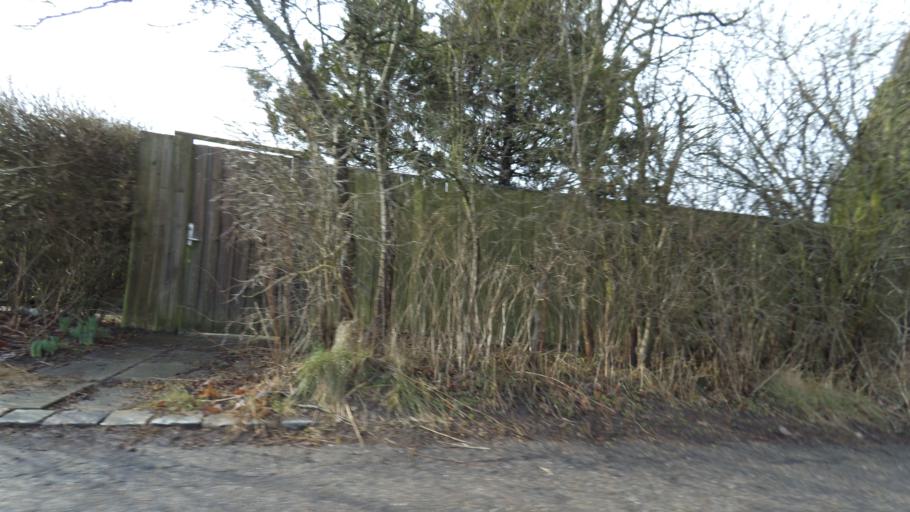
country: DK
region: Central Jutland
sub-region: Arhus Kommune
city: Arhus
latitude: 56.1690
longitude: 10.1722
